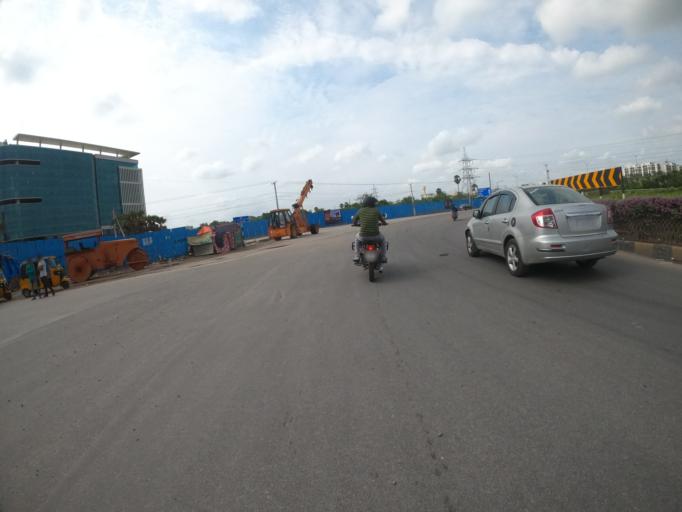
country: IN
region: Telangana
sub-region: Rangareddi
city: Kukatpalli
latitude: 17.4194
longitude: 78.3549
